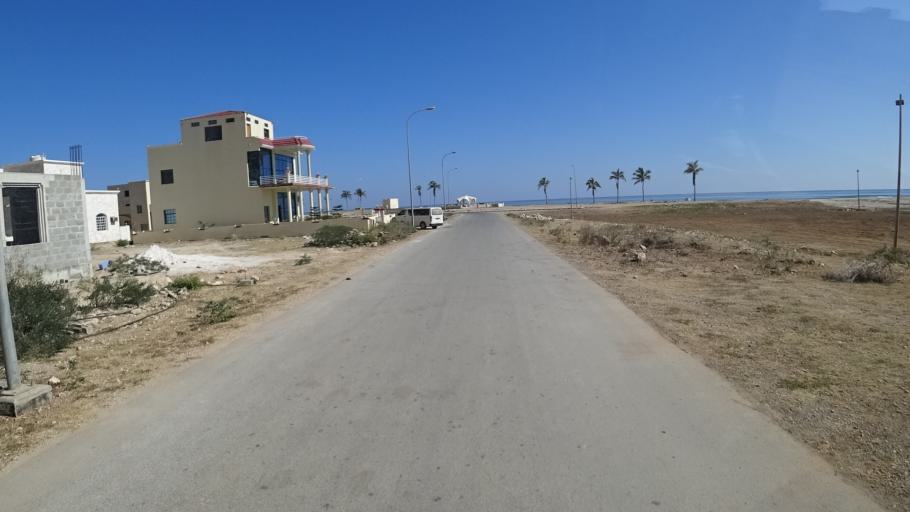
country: YE
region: Al Mahrah
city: Hawf
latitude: 16.7482
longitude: 53.4263
